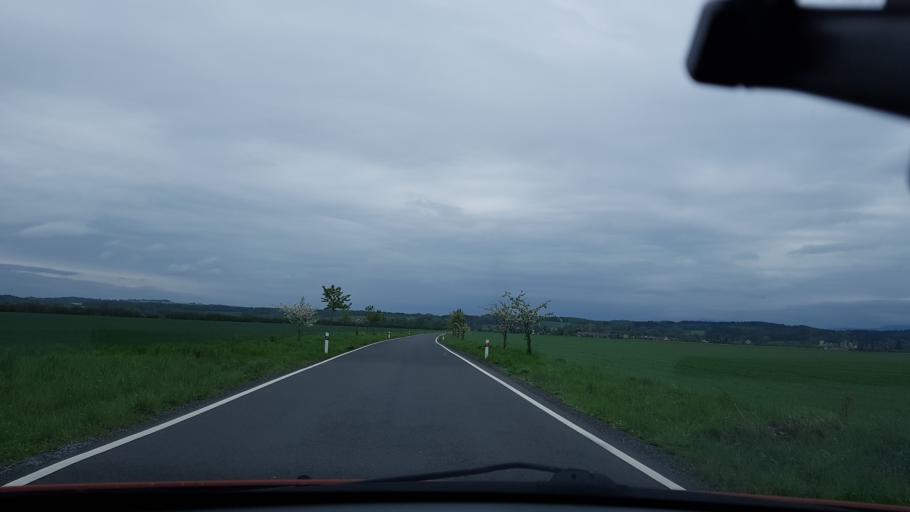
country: CZ
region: Olomoucky
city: Vidnava
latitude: 50.3798
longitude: 17.1588
